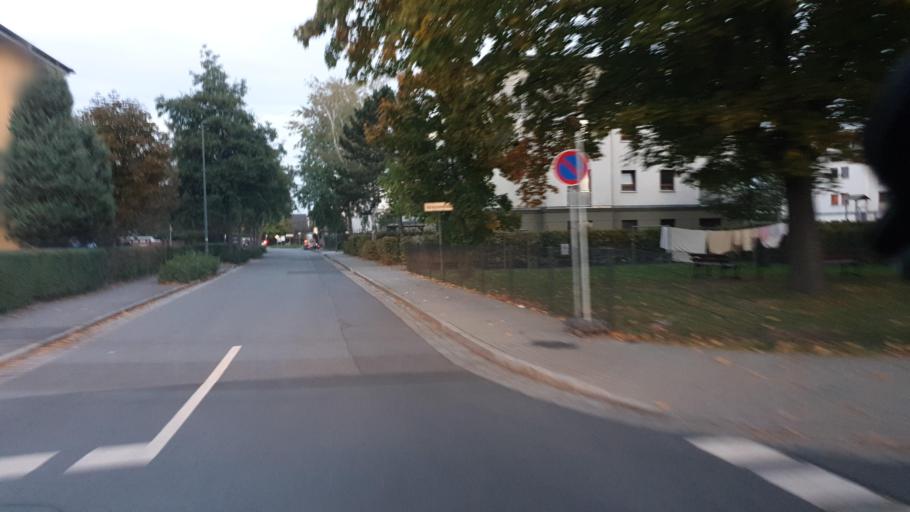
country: DE
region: Saxony
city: Radebeul
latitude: 51.1064
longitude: 13.6208
